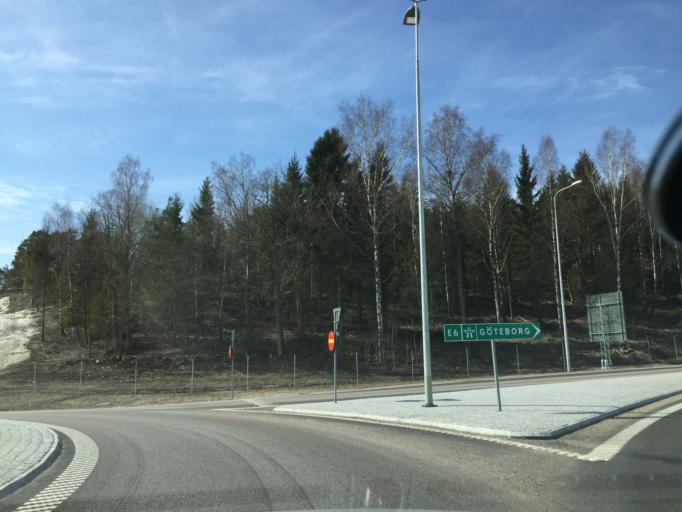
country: SE
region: Vaestra Goetaland
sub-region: Uddevalla Kommun
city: Uddevalla
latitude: 58.3567
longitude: 11.8109
